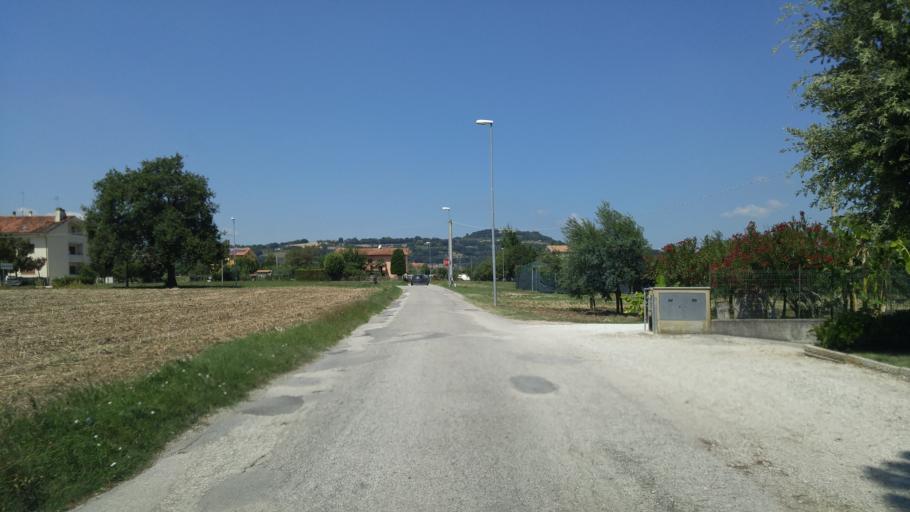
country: IT
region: The Marches
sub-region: Provincia di Pesaro e Urbino
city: Bellocchi
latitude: 43.8013
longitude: 13.0003
